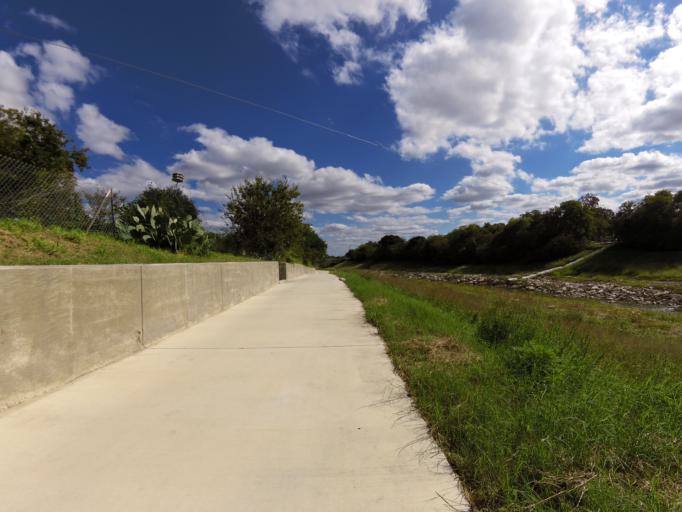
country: US
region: Texas
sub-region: Bexar County
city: San Antonio
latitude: 29.3931
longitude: -98.5023
